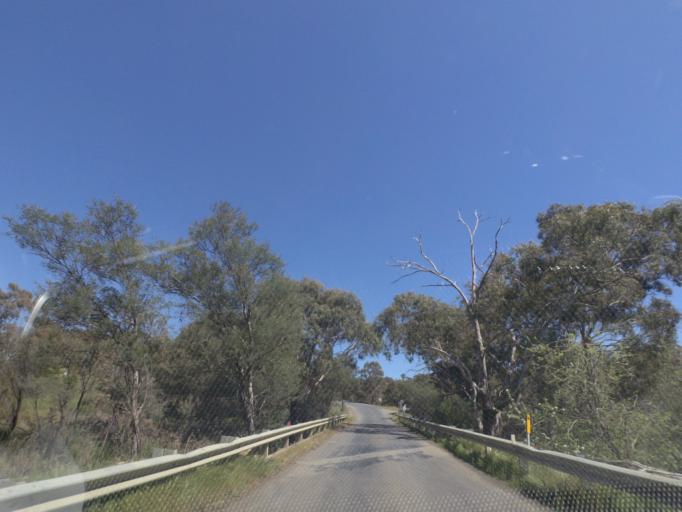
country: AU
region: Victoria
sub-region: Whittlesea
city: Whittlesea
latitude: -37.2885
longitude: 144.9818
